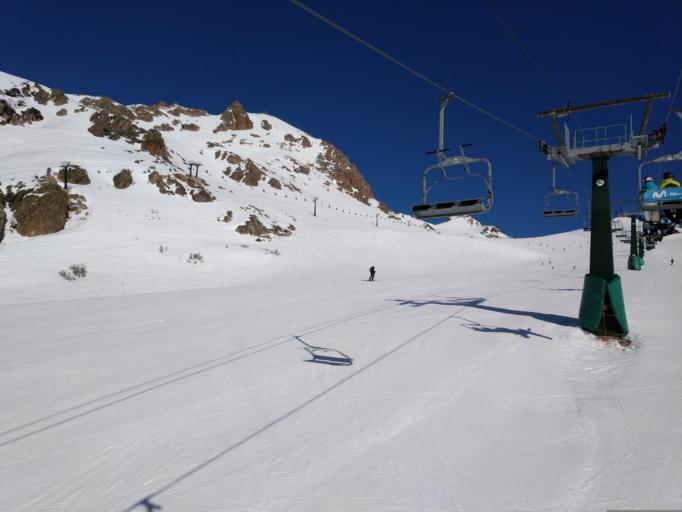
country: AR
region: Rio Negro
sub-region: Departamento de Bariloche
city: San Carlos de Bariloche
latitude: -41.1759
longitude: -71.4664
